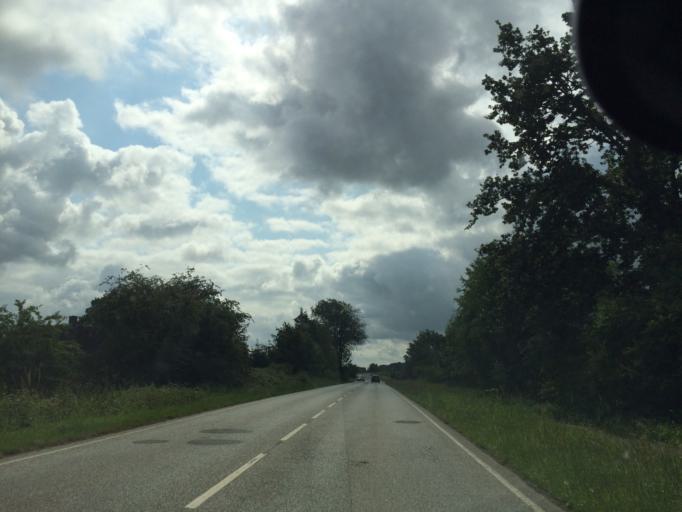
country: DE
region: Schleswig-Holstein
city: Tuttendorf
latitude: 54.4014
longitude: 9.9999
